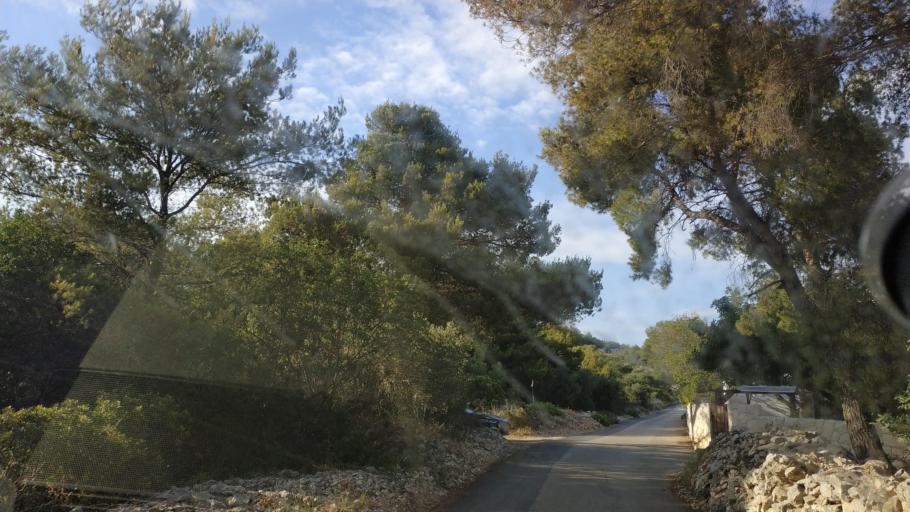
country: HR
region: Splitsko-Dalmatinska
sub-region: Grad Trogir
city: Trogir
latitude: 43.4839
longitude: 16.2444
